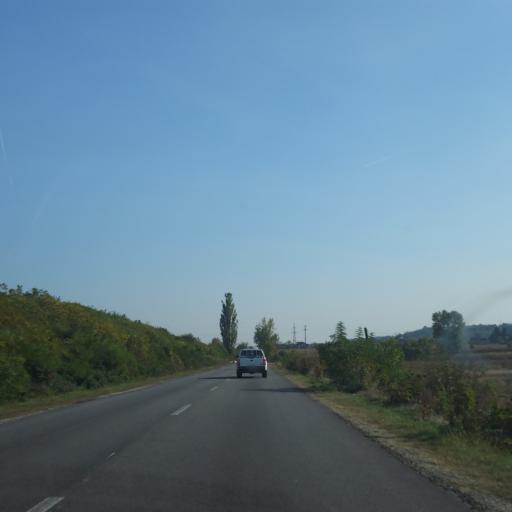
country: RO
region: Arges
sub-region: Comuna Merisani
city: Merisani
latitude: 44.9559
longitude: 24.7581
